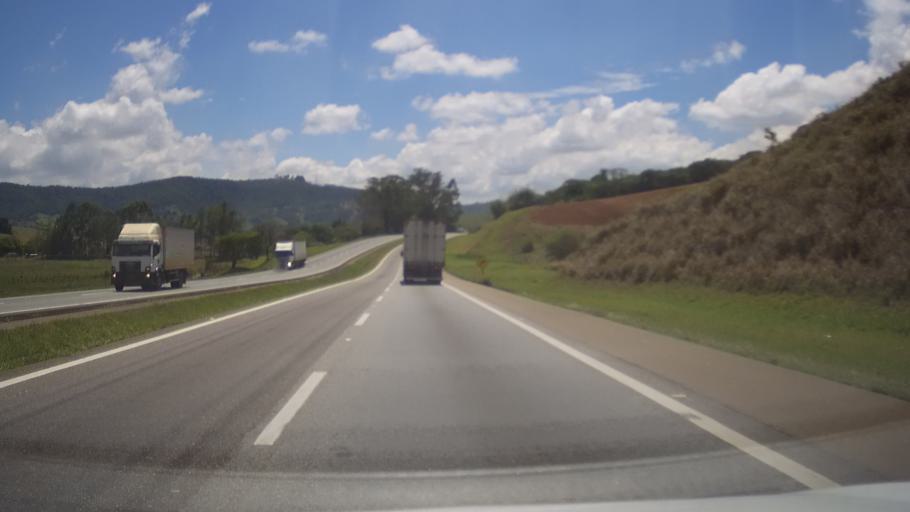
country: BR
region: Minas Gerais
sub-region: Campanha
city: Campanha
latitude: -21.8278
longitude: -45.4968
